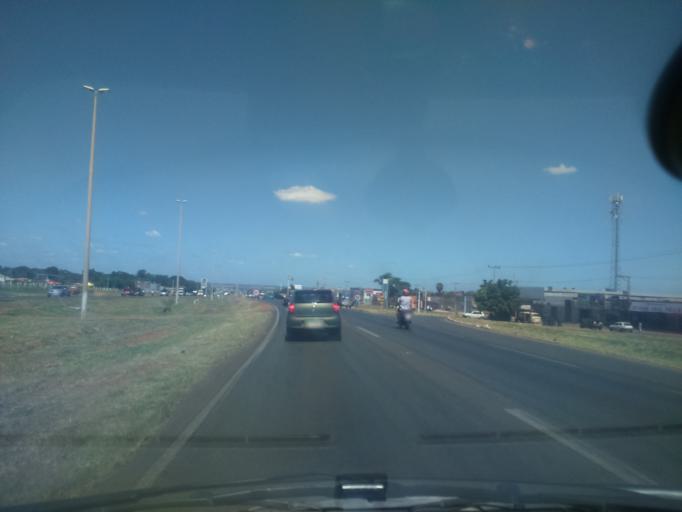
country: BR
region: Goias
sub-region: Luziania
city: Luziania
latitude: -16.0867
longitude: -47.9863
